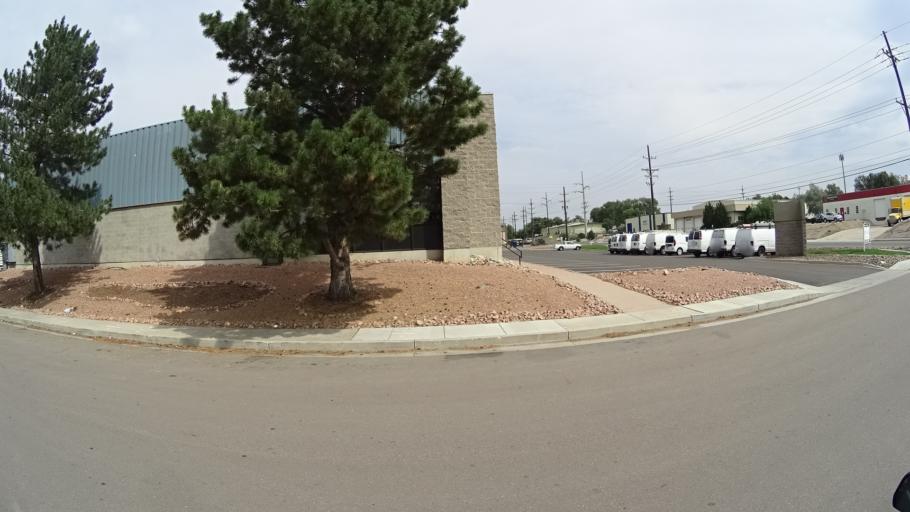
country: US
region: Colorado
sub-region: El Paso County
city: Colorado Springs
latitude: 38.8800
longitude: -104.8233
